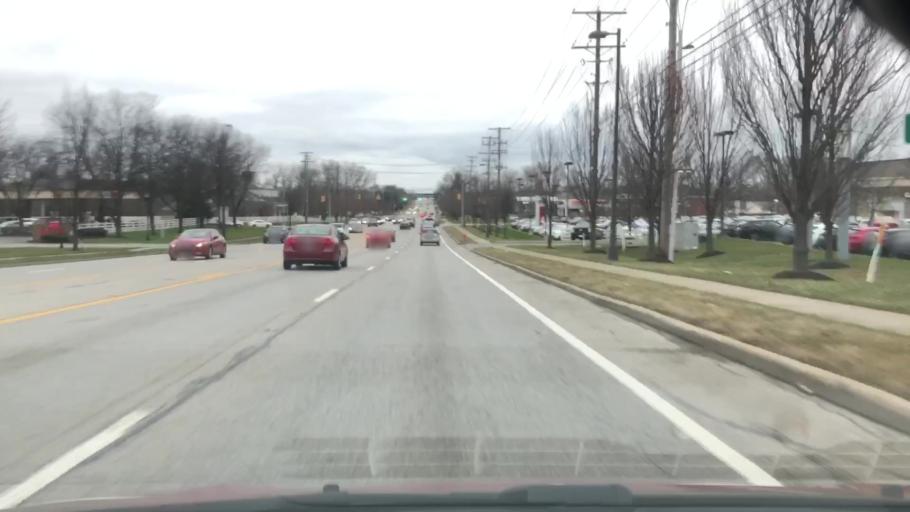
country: US
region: Ohio
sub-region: Franklin County
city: Gahanna
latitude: 40.0563
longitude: -82.8842
